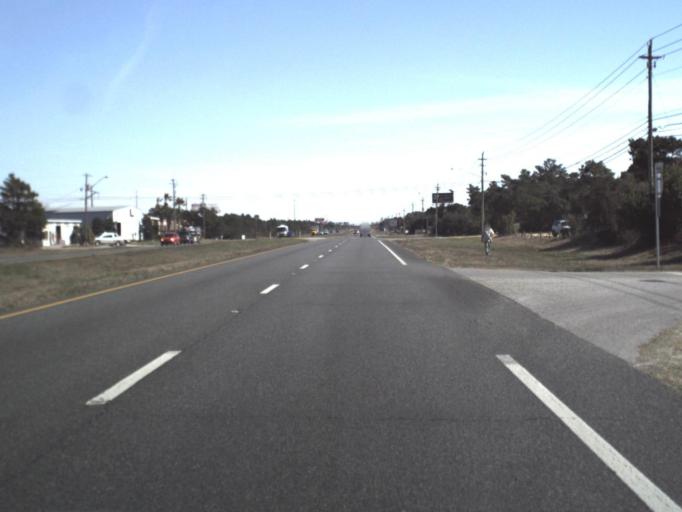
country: US
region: Florida
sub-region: Bay County
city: Laguna Beach
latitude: 30.2470
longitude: -85.9264
